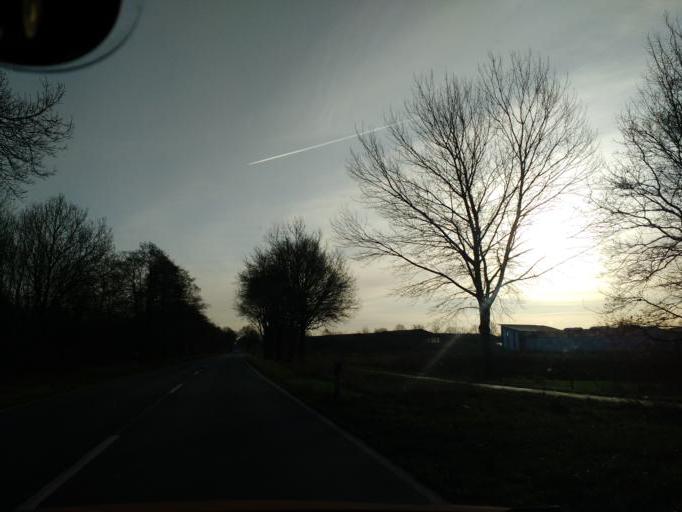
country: DE
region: Lower Saxony
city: Oldenburg
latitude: 53.1345
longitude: 8.2851
